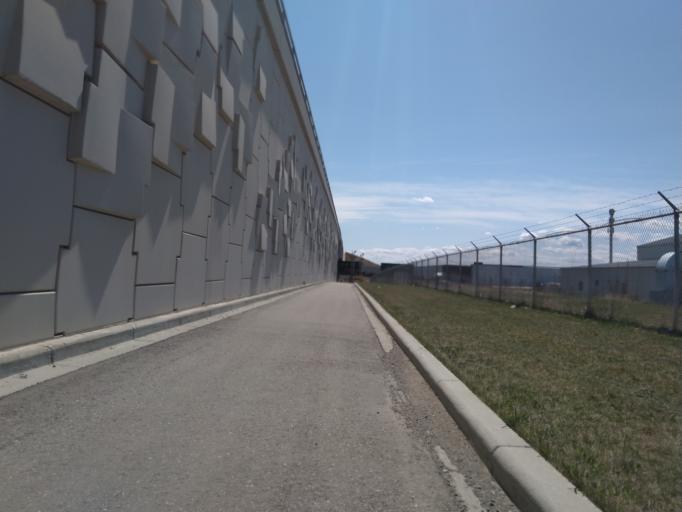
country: CA
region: Alberta
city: Calgary
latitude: 50.9648
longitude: -113.9587
